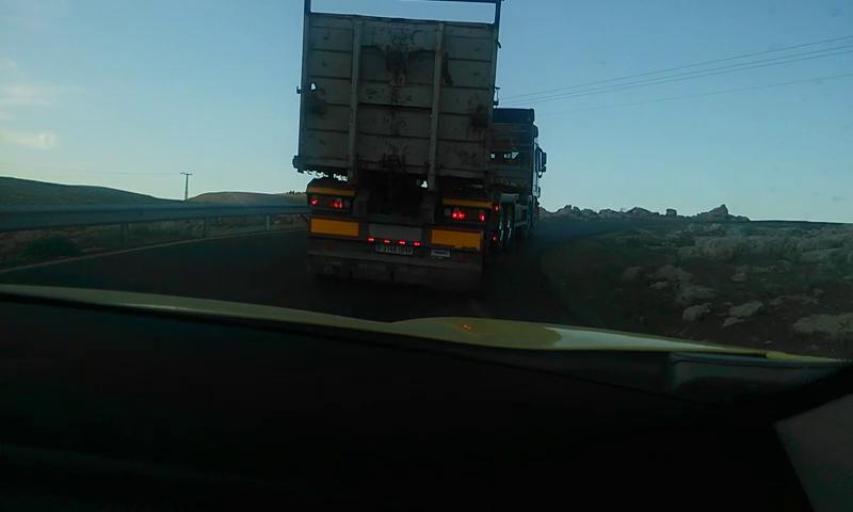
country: PS
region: West Bank
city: Rammun
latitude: 31.9168
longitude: 35.3476
